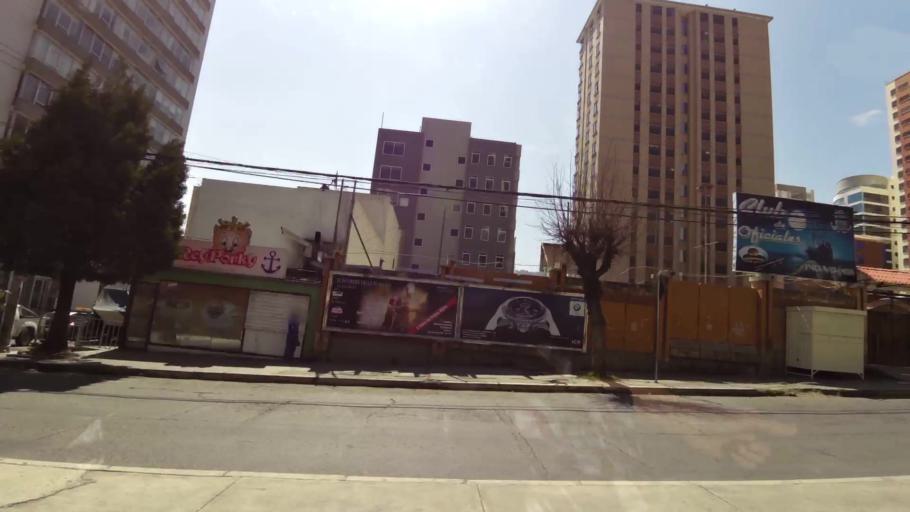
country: BO
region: La Paz
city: La Paz
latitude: -16.5390
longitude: -68.0766
